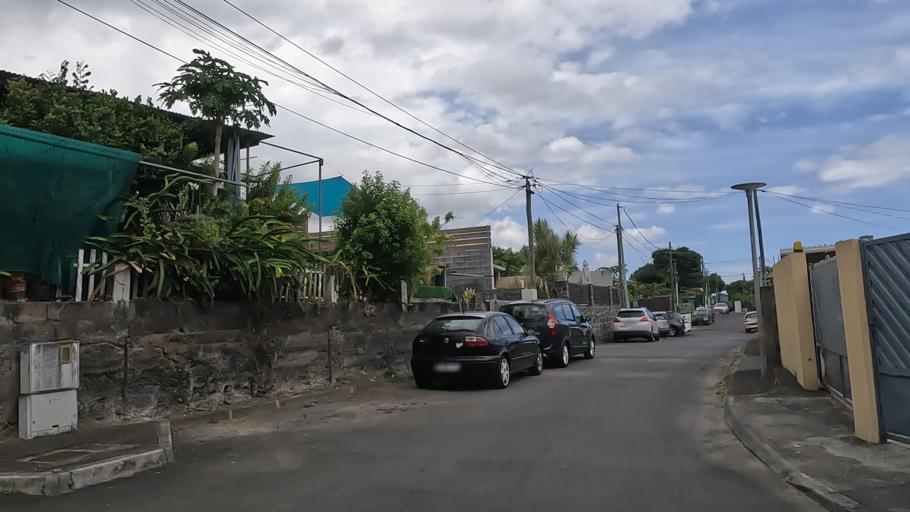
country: RE
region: Reunion
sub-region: Reunion
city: La Possession
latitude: -20.9595
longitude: 55.3364
